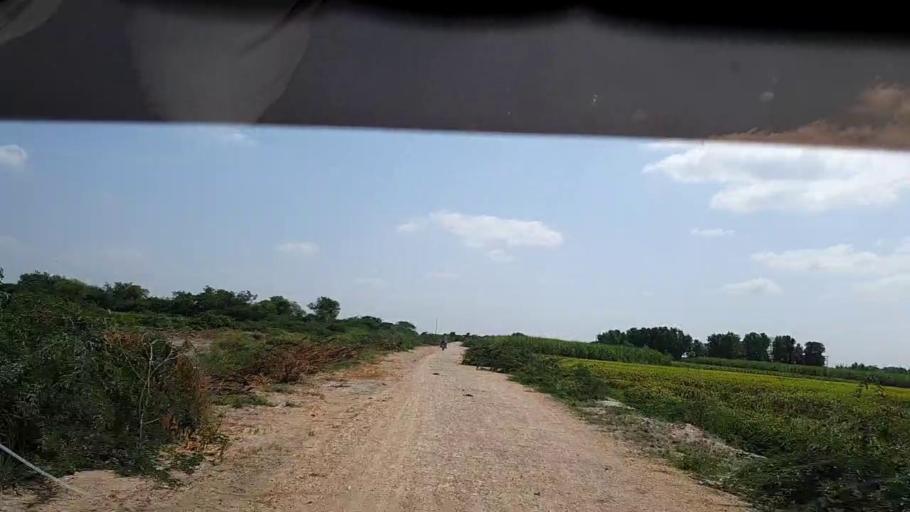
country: PK
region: Sindh
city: Kadhan
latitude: 24.5917
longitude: 68.9921
